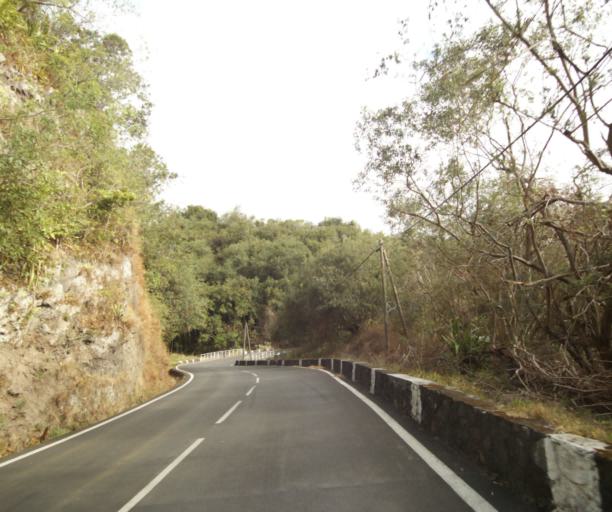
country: RE
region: Reunion
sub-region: Reunion
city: Saint-Paul
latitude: -21.0170
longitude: 55.3184
